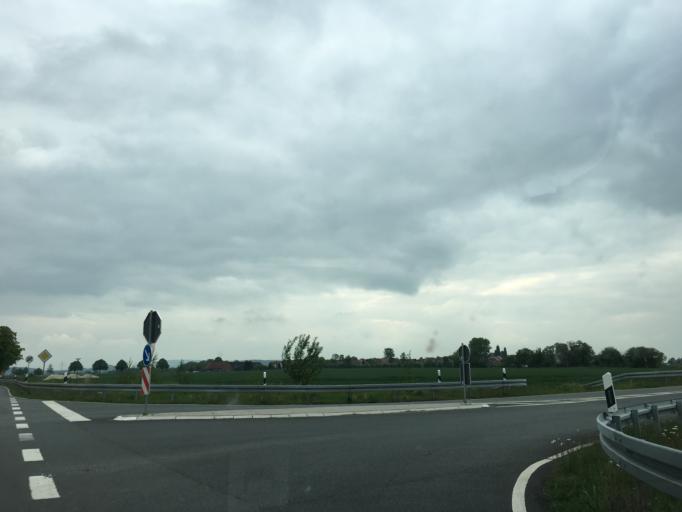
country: DE
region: Lower Saxony
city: Haste
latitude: 52.3734
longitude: 9.3848
